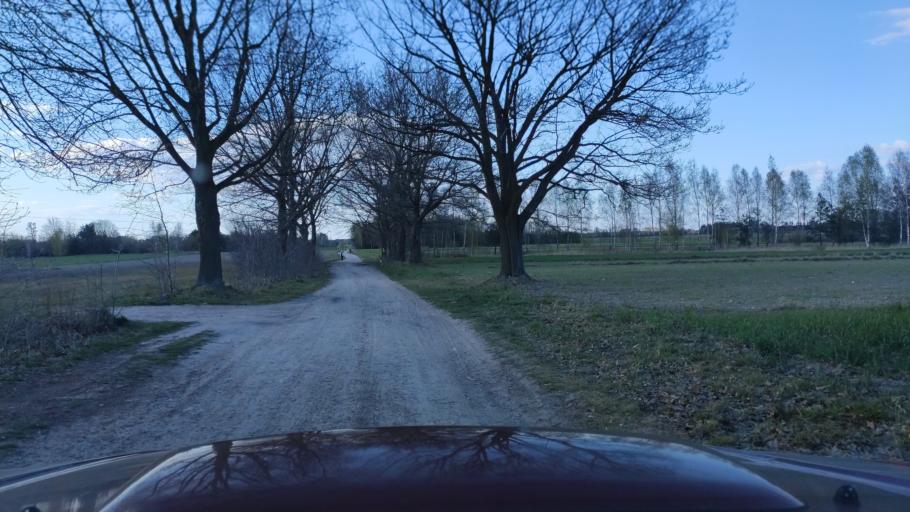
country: PL
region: Masovian Voivodeship
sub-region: Powiat zwolenski
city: Zwolen
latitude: 51.3653
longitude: 21.5757
